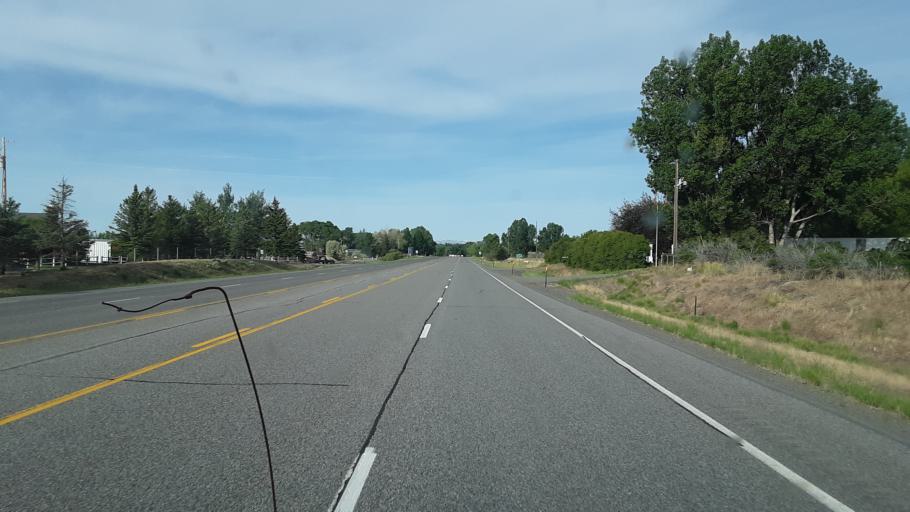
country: US
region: Wyoming
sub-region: Fremont County
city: Riverton
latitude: 43.0887
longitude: -108.3711
